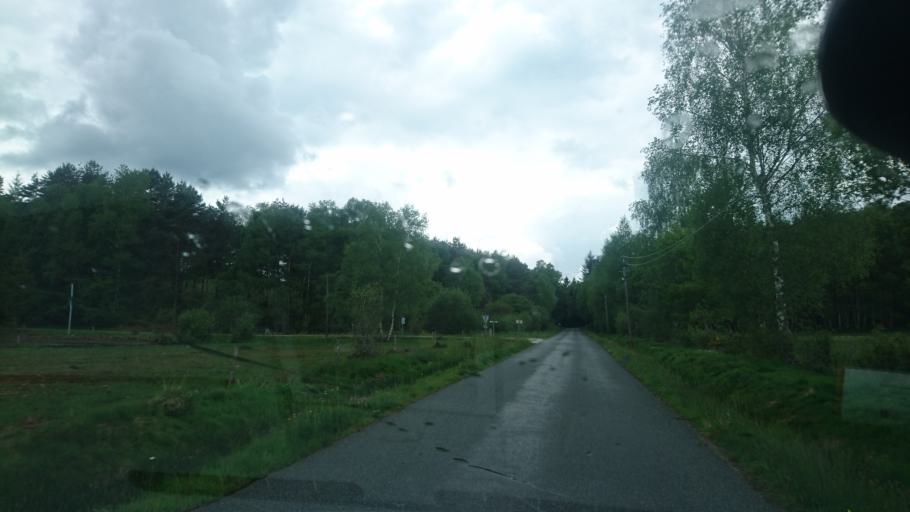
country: FR
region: Limousin
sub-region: Departement de la Haute-Vienne
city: Peyrat-le-Chateau
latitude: 45.8308
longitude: 1.8529
